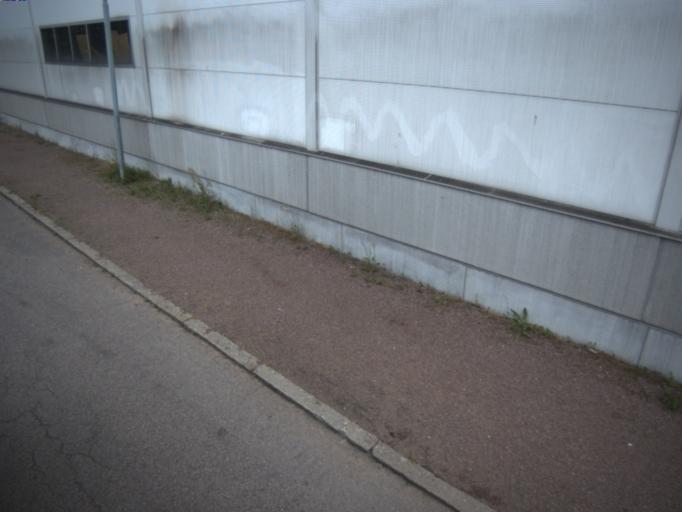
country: SE
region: Skane
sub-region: Helsingborg
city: Helsingborg
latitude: 56.0309
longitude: 12.7136
